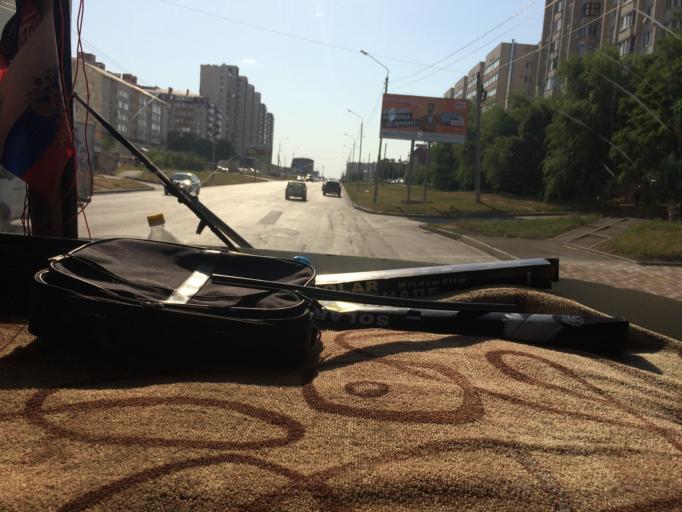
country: RU
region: Stavropol'skiy
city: Tatarka
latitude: 44.9991
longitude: 41.9171
